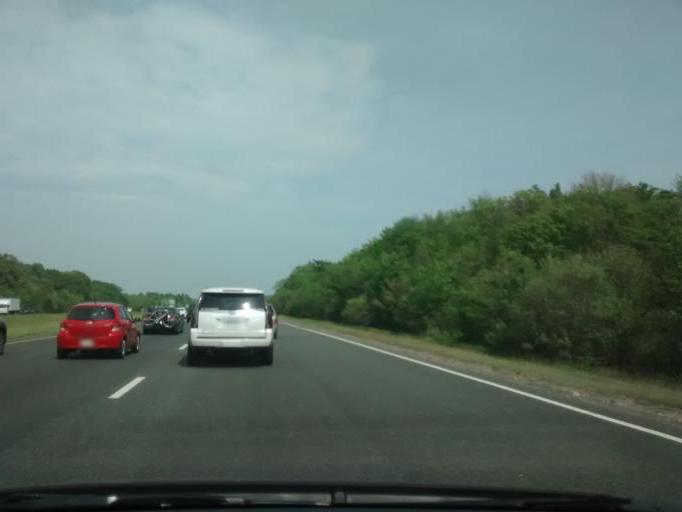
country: US
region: Massachusetts
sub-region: Bristol County
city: Raynham
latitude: 41.9584
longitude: -71.0633
